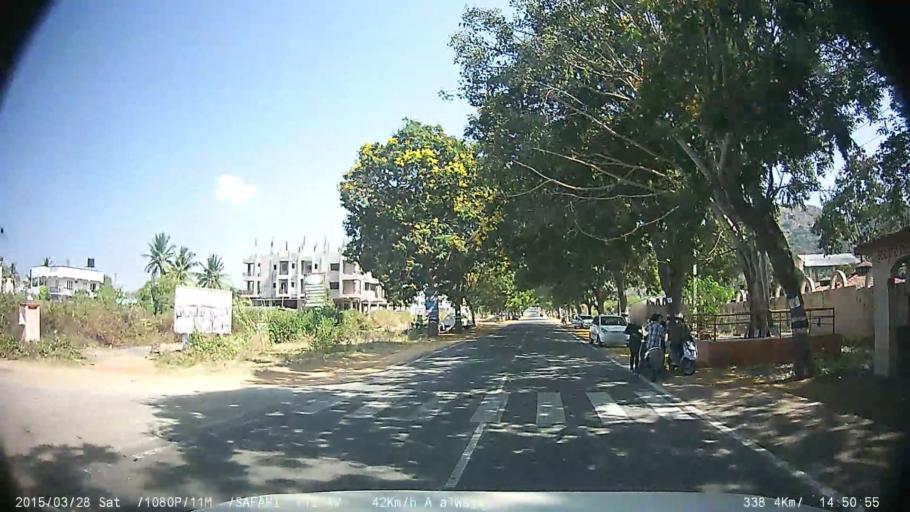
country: IN
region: Karnataka
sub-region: Mysore
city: Mysore
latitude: 12.2930
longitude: 76.6829
